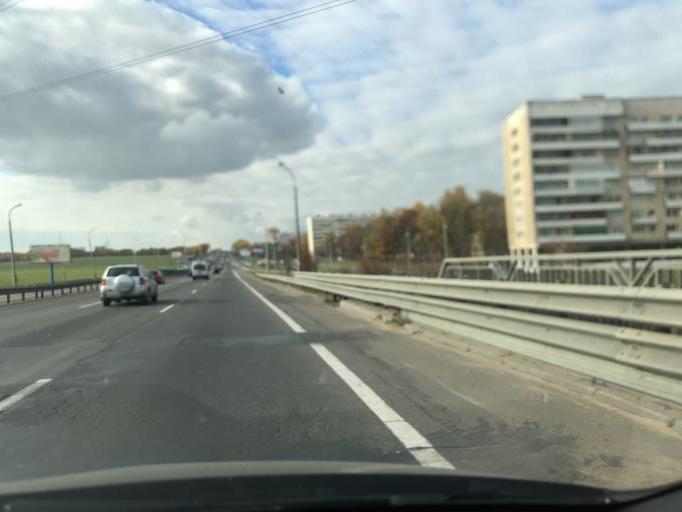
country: BY
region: Minsk
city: Yubilyeyny
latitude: 53.8389
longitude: 27.5029
